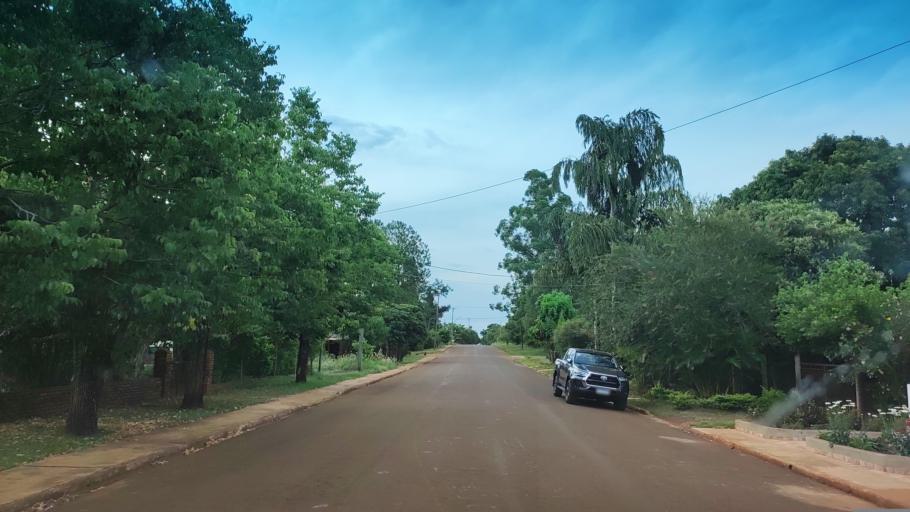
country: AR
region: Misiones
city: Gobernador Roca
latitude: -27.1286
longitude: -55.5138
